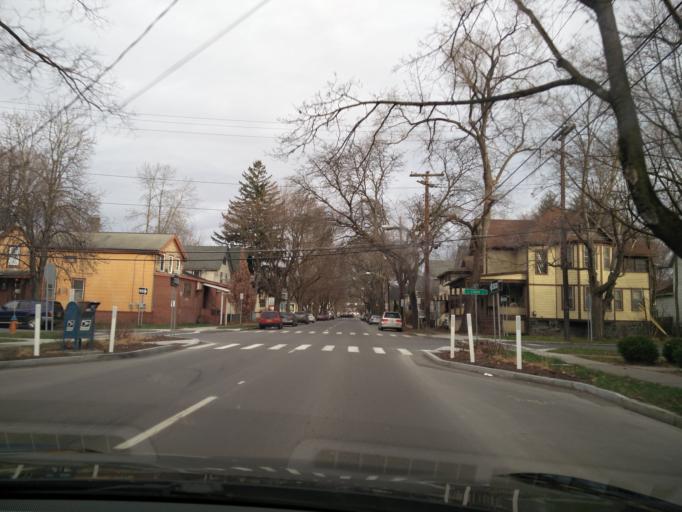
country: US
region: New York
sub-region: Tompkins County
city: Ithaca
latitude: 42.4384
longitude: -76.5065
